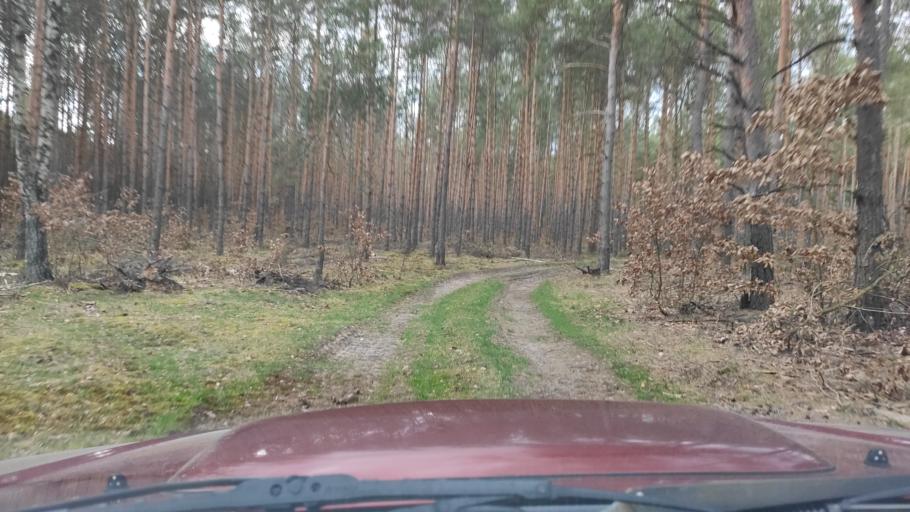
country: PL
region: Masovian Voivodeship
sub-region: Powiat kozienicki
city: Garbatka-Letnisko
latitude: 51.5134
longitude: 21.5690
